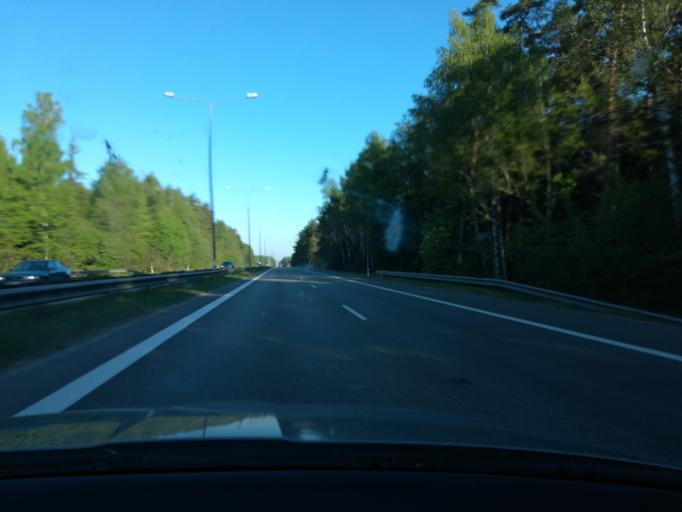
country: LT
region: Kauno apskritis
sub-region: Kauno rajonas
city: Karmelava
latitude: 54.8923
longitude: 24.1600
